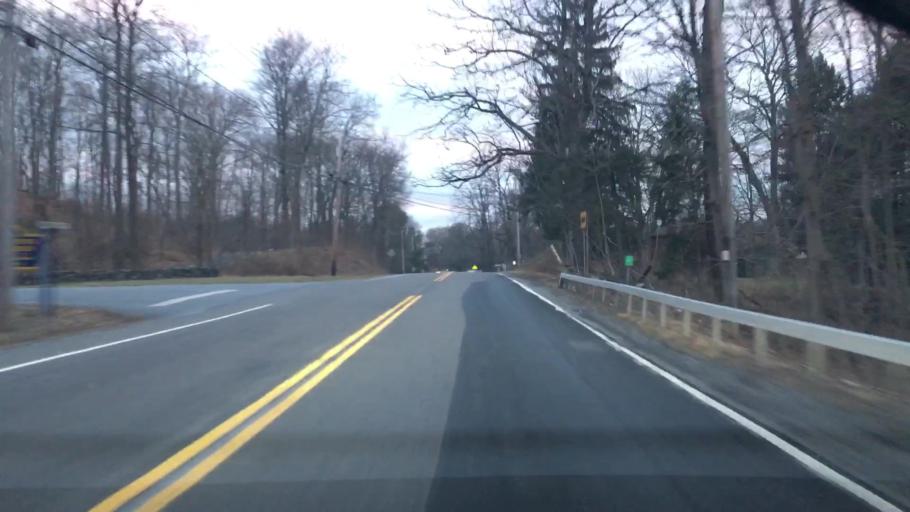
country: US
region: New York
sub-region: Dutchess County
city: Red Oaks Mill
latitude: 41.6671
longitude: -73.8787
